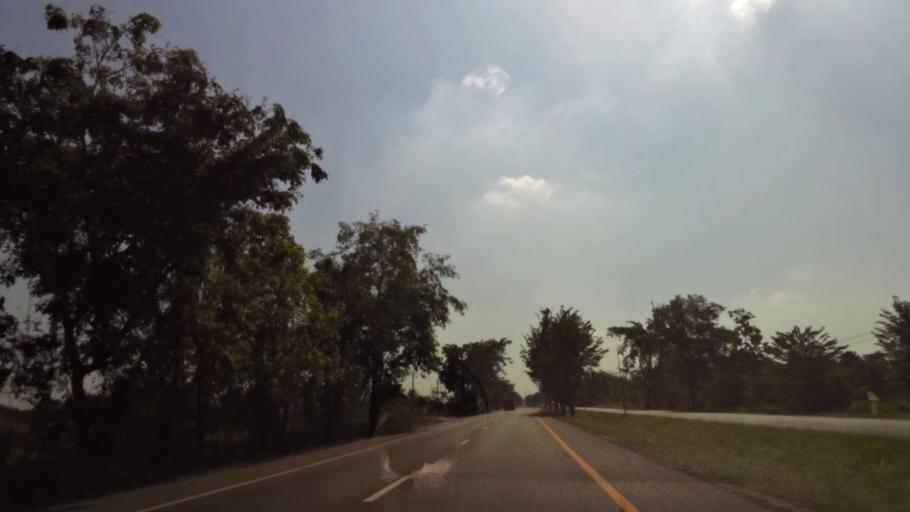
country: TH
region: Phichit
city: Bueng Na Rang
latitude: 16.2226
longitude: 100.1264
